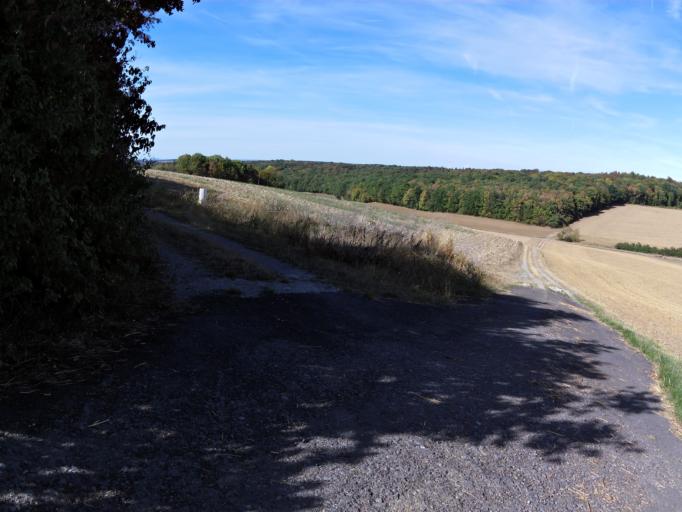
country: DE
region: Bavaria
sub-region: Regierungsbezirk Unterfranken
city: Eisingen
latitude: 49.7630
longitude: 9.8303
